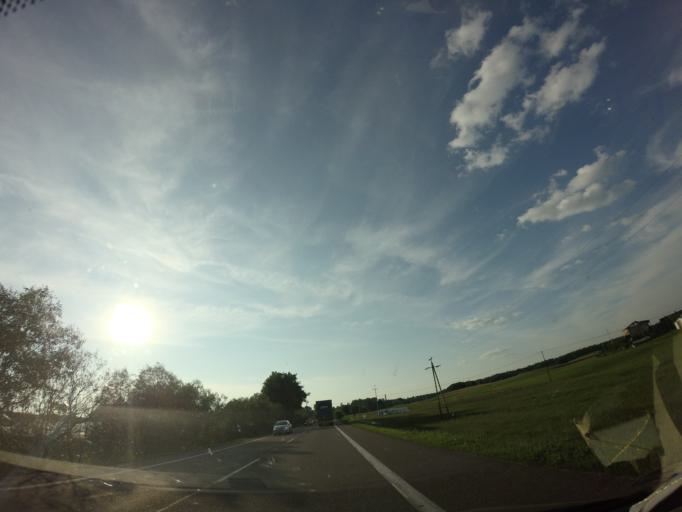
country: PL
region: Podlasie
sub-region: Powiat augustowski
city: Augustow
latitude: 53.7922
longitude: 22.9879
